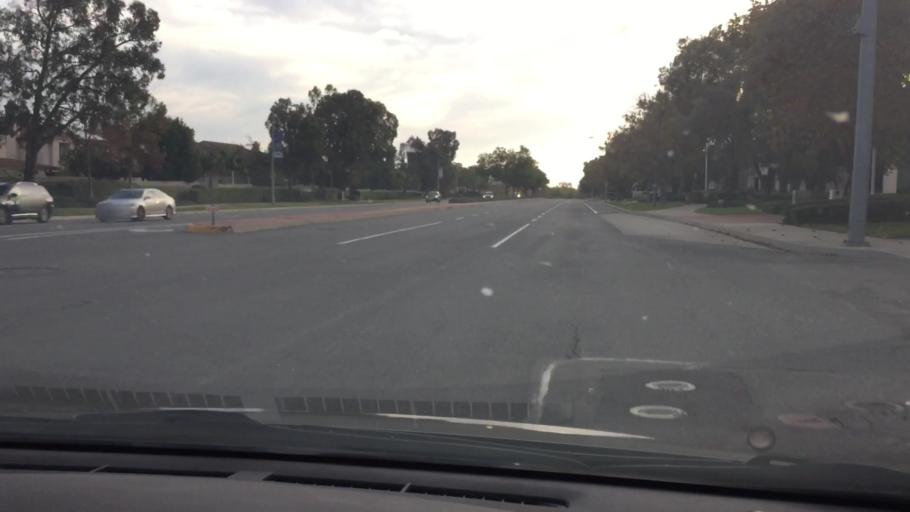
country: US
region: California
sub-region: Orange County
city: Rancho Santa Margarita
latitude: 33.6264
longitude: -117.6064
